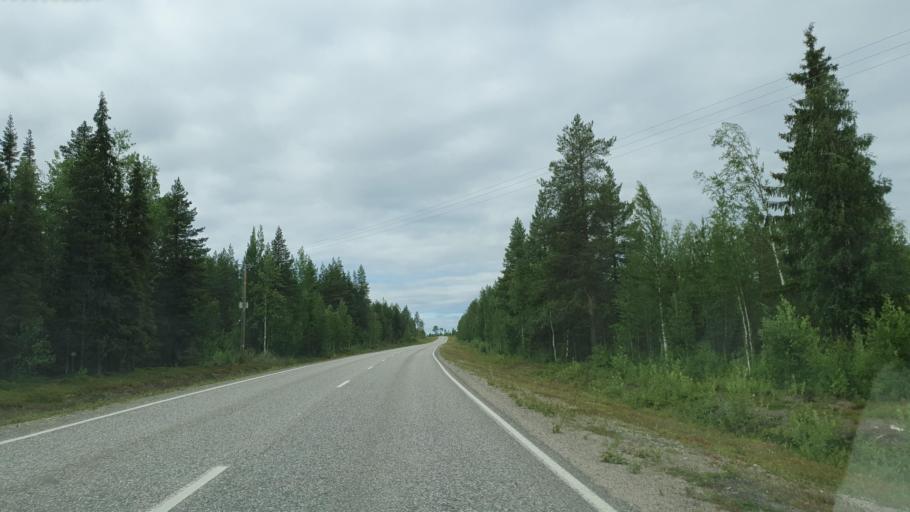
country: FI
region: Lapland
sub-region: Tunturi-Lappi
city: Kittilae
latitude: 67.6611
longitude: 24.8237
